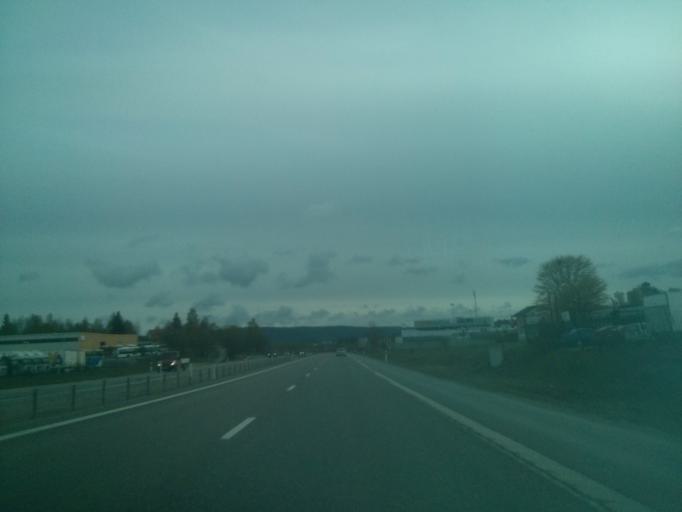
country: SE
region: Vaesternorrland
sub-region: Sundsvalls Kommun
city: Johannedal
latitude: 62.4177
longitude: 17.3448
